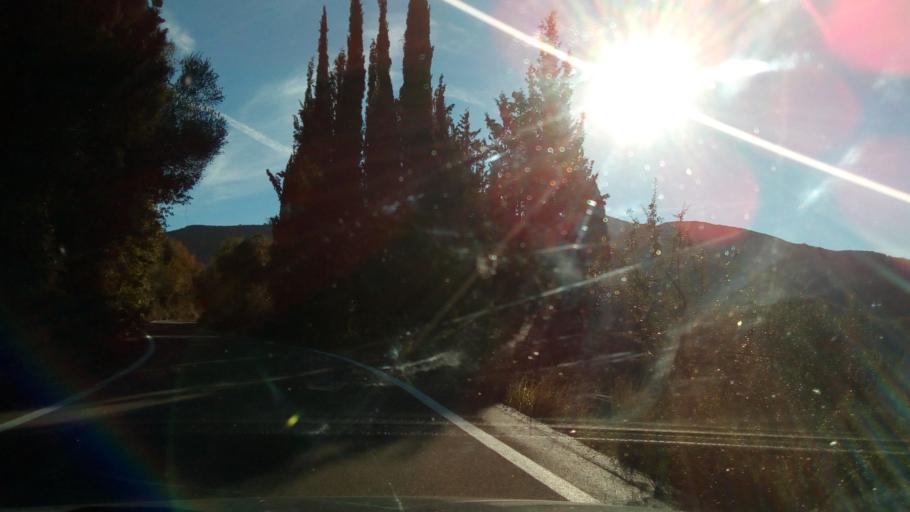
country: GR
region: West Greece
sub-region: Nomos Aitolias kai Akarnanias
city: Nafpaktos
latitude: 38.4673
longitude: 21.8782
